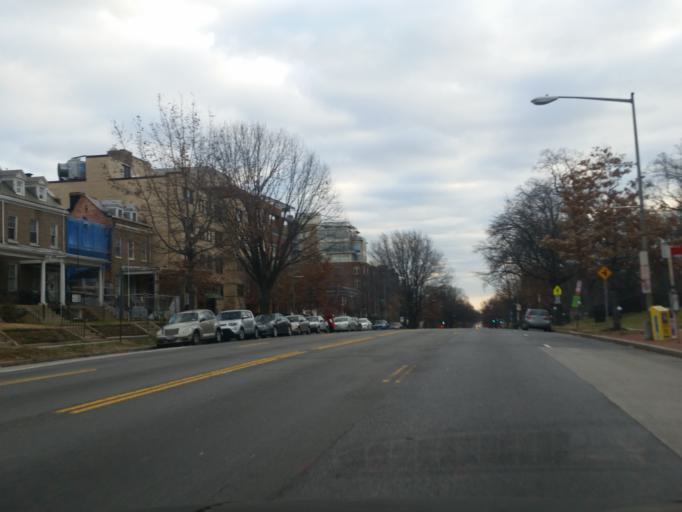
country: US
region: Maryland
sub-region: Montgomery County
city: Chevy Chase Village
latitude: 38.9430
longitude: -77.0628
